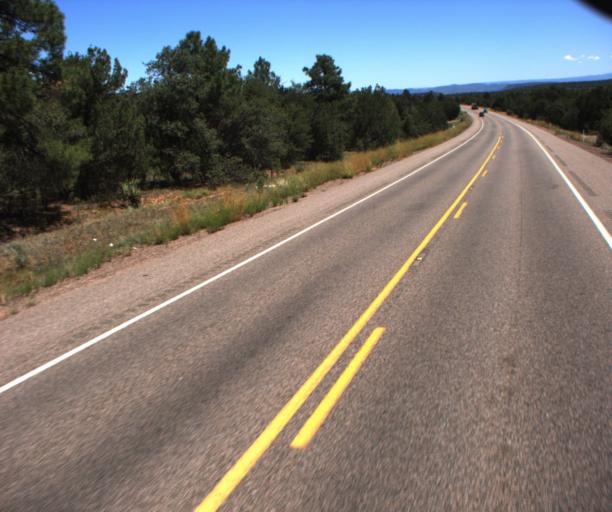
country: US
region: Arizona
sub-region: Navajo County
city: Cibecue
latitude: 33.7015
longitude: -110.5438
